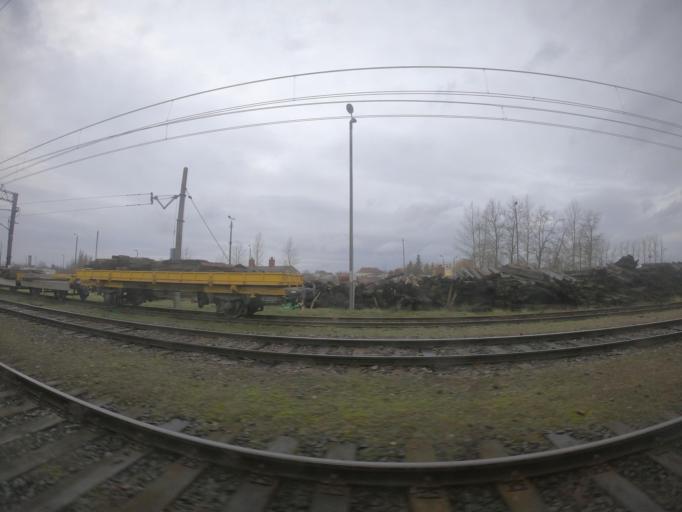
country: PL
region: West Pomeranian Voivodeship
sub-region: Powiat szczecinecki
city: Szczecinek
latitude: 53.6989
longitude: 16.7139
